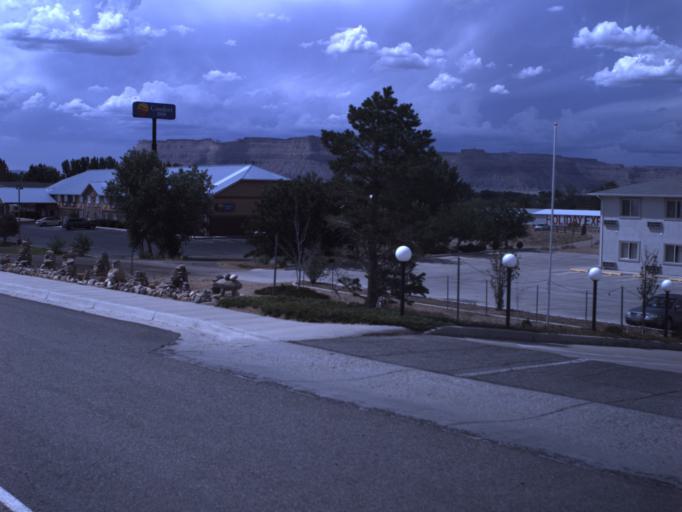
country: US
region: Utah
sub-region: Carbon County
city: East Carbon City
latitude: 38.9922
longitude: -110.1366
